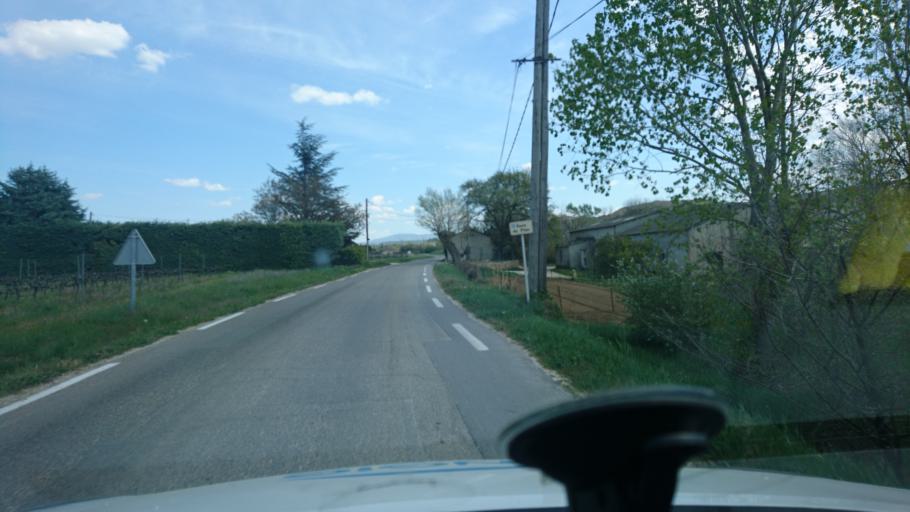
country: FR
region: Provence-Alpes-Cote d'Azur
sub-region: Departement du Vaucluse
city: Maubec
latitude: 43.8592
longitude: 5.1476
